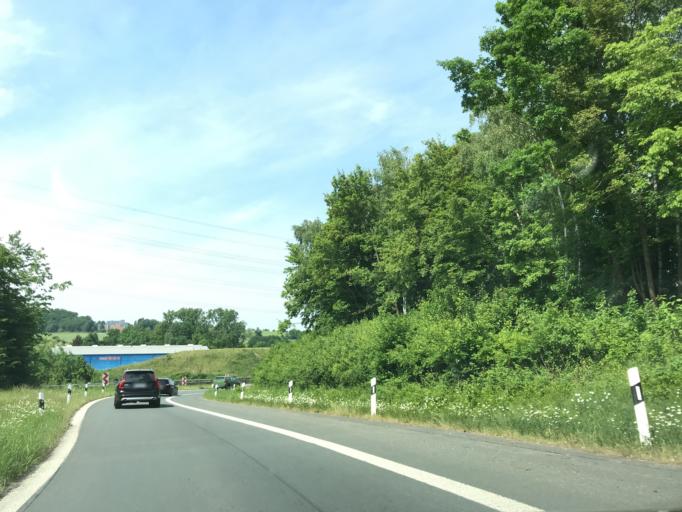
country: DE
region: North Rhine-Westphalia
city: Witten
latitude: 51.4354
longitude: 7.2906
